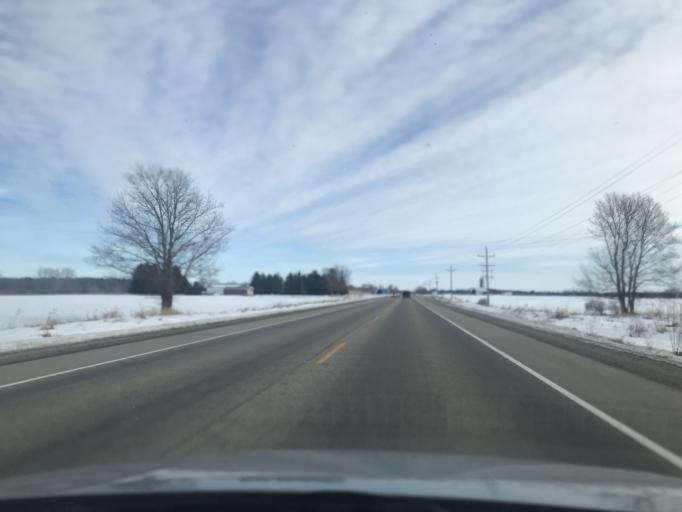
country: US
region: Wisconsin
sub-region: Oconto County
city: Gillett
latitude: 44.8962
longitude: -88.2652
